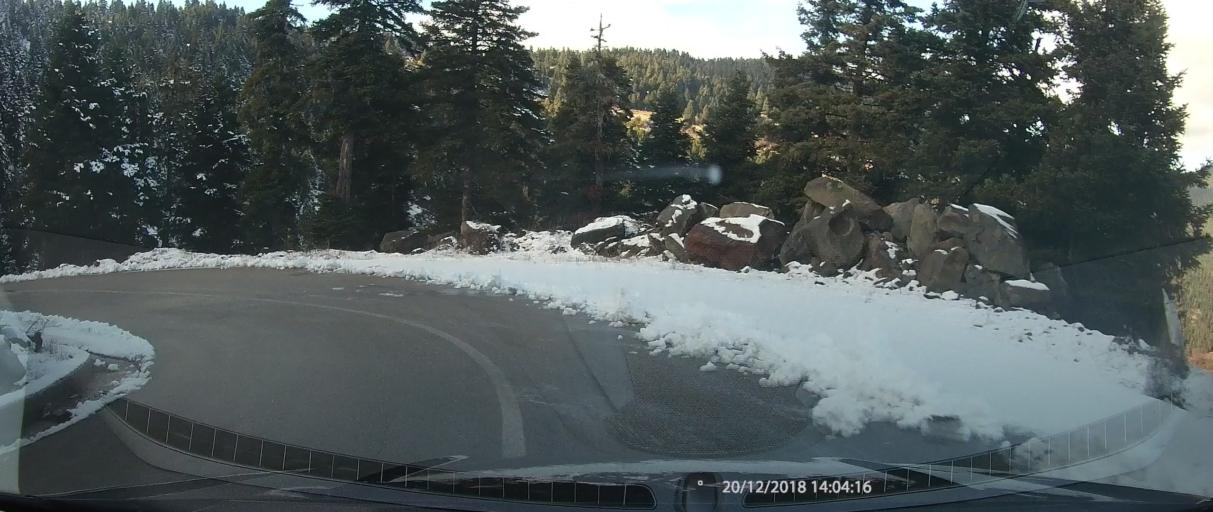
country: GR
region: West Greece
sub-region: Nomos Aitolias kai Akarnanias
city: Thermo
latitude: 38.7431
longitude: 21.6417
